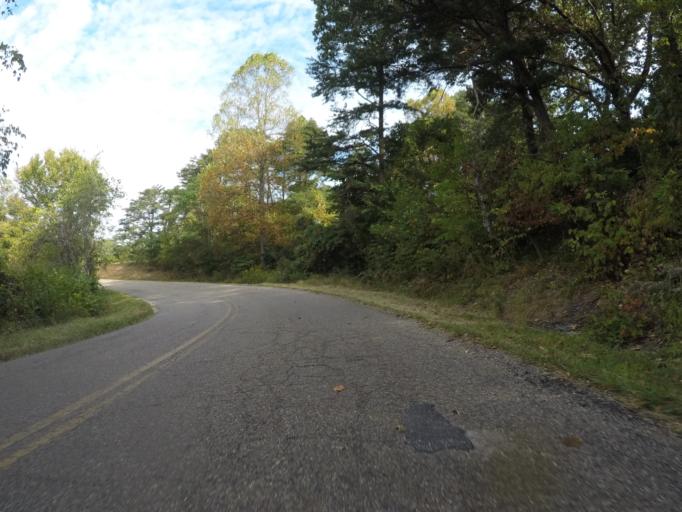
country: US
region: West Virginia
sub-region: Cabell County
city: Lesage
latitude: 38.5626
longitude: -82.4259
